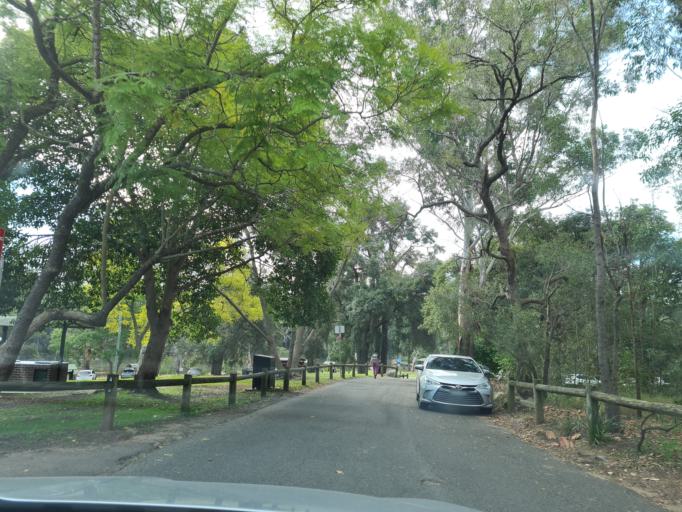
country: AU
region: New South Wales
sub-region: Parramatta
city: Northmead
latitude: -33.7917
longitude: 151.0079
